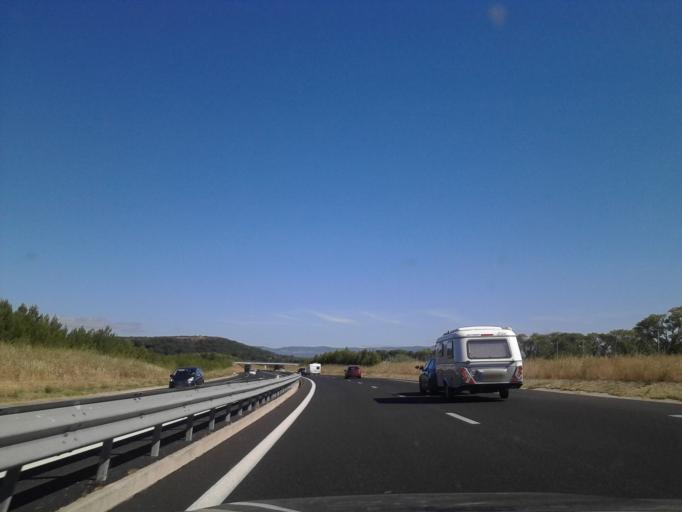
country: FR
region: Languedoc-Roussillon
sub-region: Departement de l'Herault
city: Aspiran
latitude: 43.5646
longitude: 3.4665
